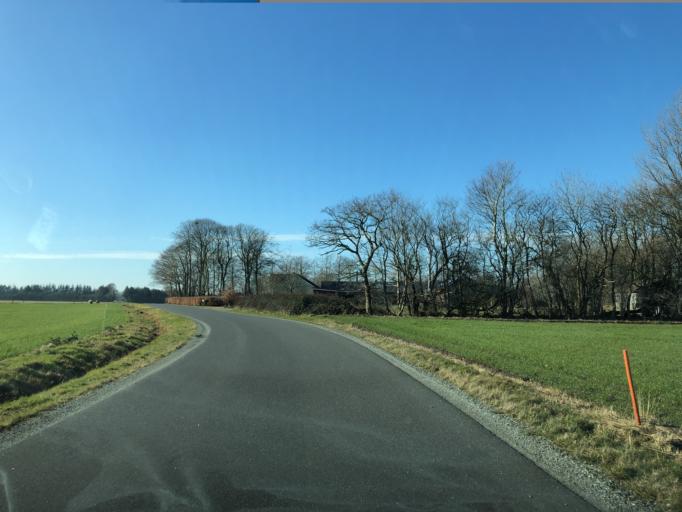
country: DK
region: Central Jutland
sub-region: Ikast-Brande Kommune
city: Bording Kirkeby
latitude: 56.1567
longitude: 9.3237
